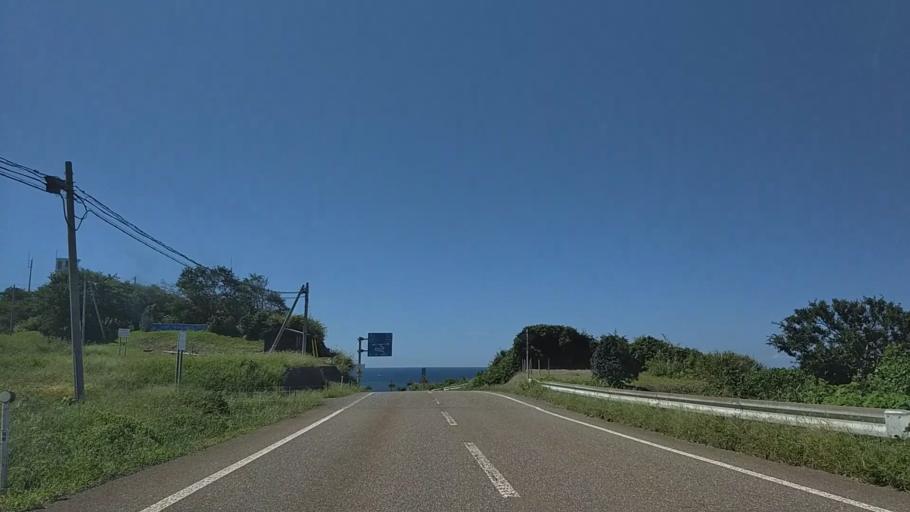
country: JP
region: Niigata
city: Joetsu
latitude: 37.1724
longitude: 138.0979
